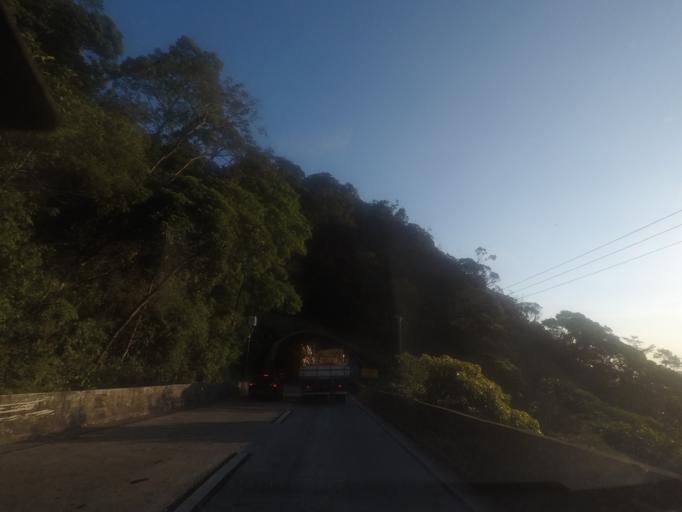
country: BR
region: Rio de Janeiro
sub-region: Petropolis
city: Petropolis
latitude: -22.5226
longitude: -43.2378
